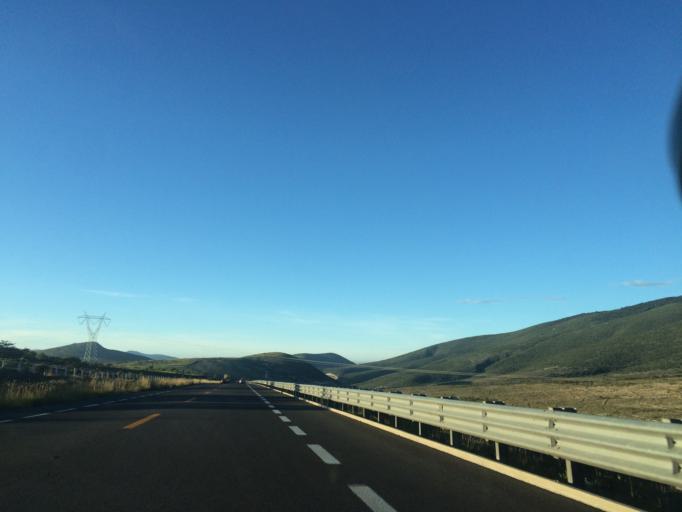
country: MX
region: Puebla
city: Morelos Canada
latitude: 18.6965
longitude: -97.4642
